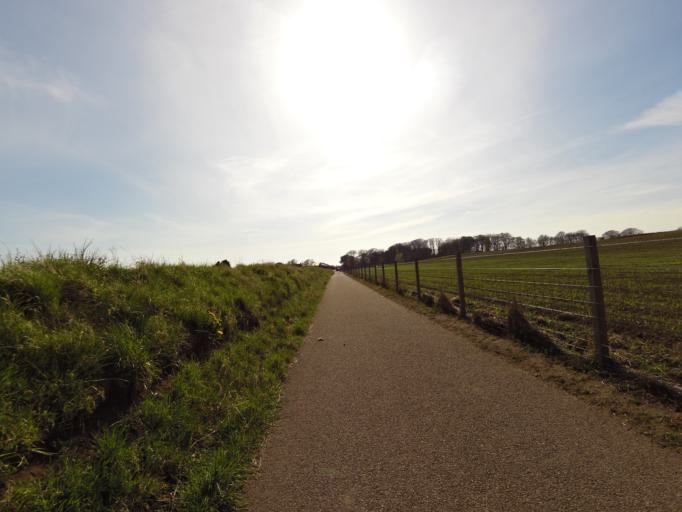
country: GB
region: Scotland
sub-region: Angus
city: Carnoustie
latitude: 56.5092
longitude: -2.6805
